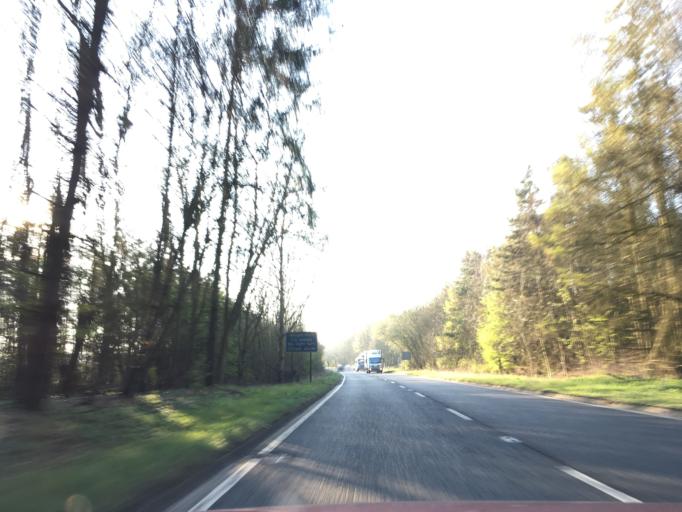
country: GB
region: England
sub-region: Gloucestershire
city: Northleach
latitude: 51.8283
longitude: -1.8113
